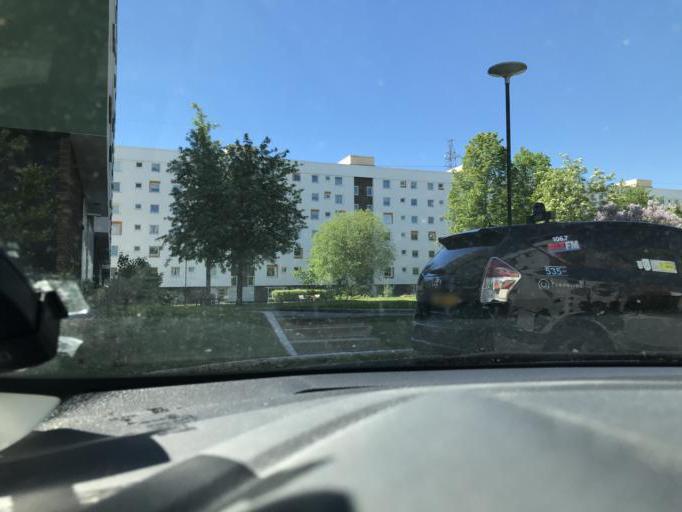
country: SE
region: Stockholm
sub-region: Botkyrka Kommun
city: Alby
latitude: 59.2372
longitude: 17.8405
